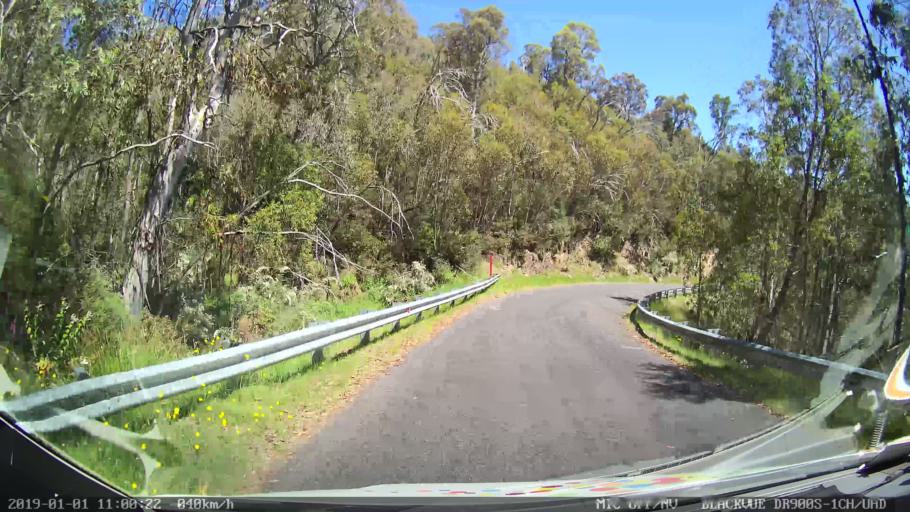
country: AU
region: New South Wales
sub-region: Snowy River
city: Jindabyne
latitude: -35.9811
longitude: 148.3970
